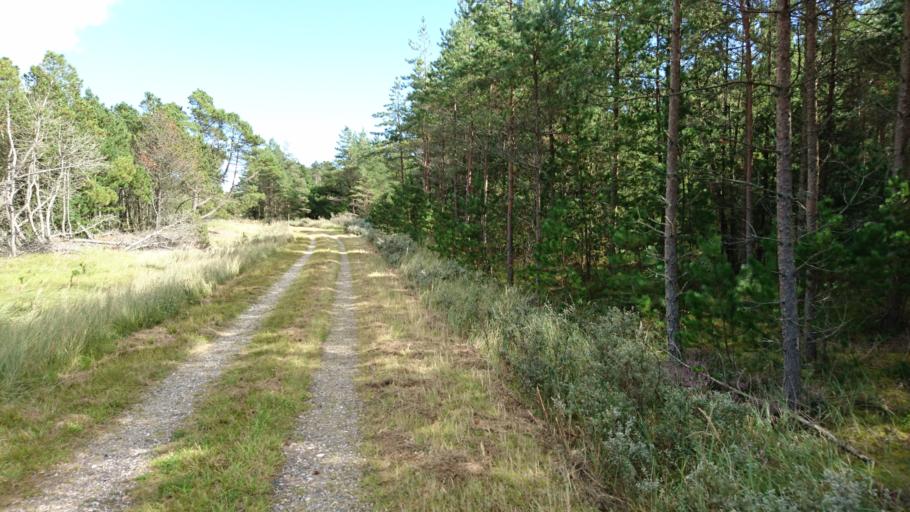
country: DK
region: North Denmark
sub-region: Frederikshavn Kommune
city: Skagen
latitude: 57.7072
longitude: 10.5097
